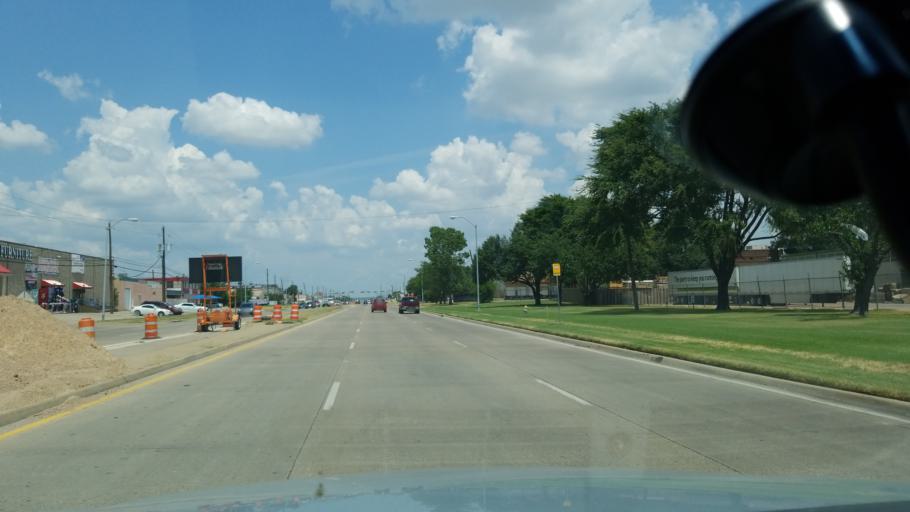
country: US
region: Texas
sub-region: Dallas County
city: Farmers Branch
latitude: 32.8708
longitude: -96.8829
